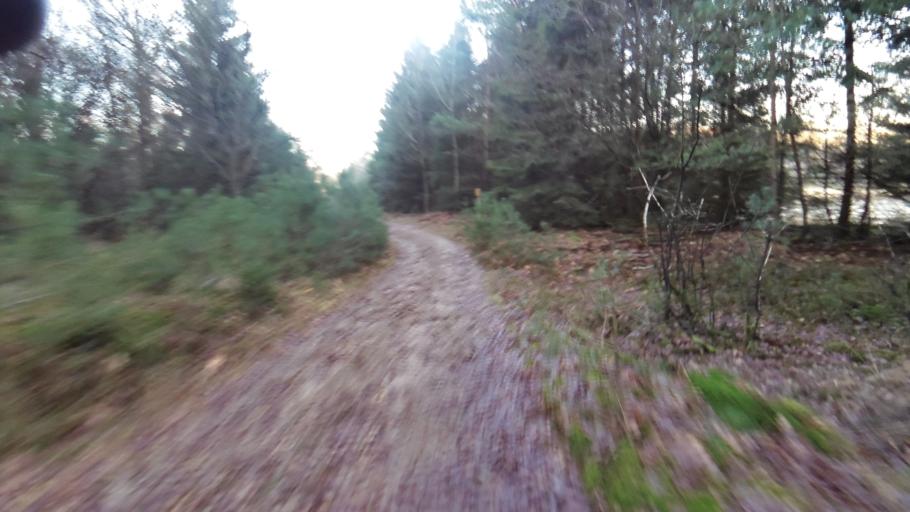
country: NL
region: Gelderland
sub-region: Gemeente Apeldoorn
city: Uddel
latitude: 52.2069
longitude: 5.7940
